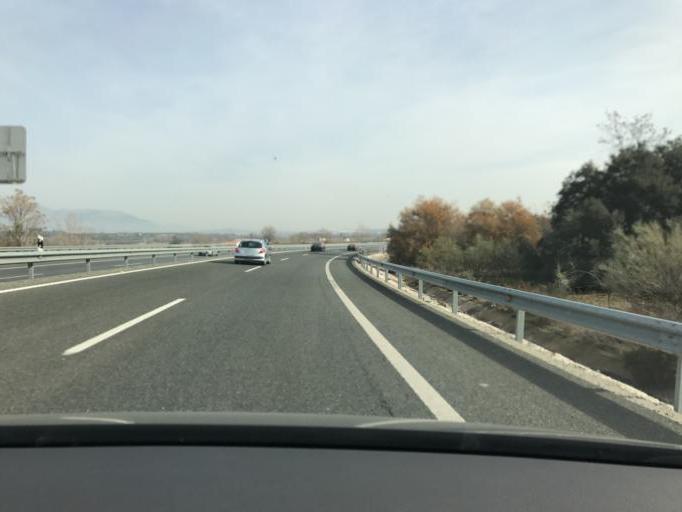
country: ES
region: Andalusia
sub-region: Provincia de Granada
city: Salar
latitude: 37.1806
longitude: -4.0782
